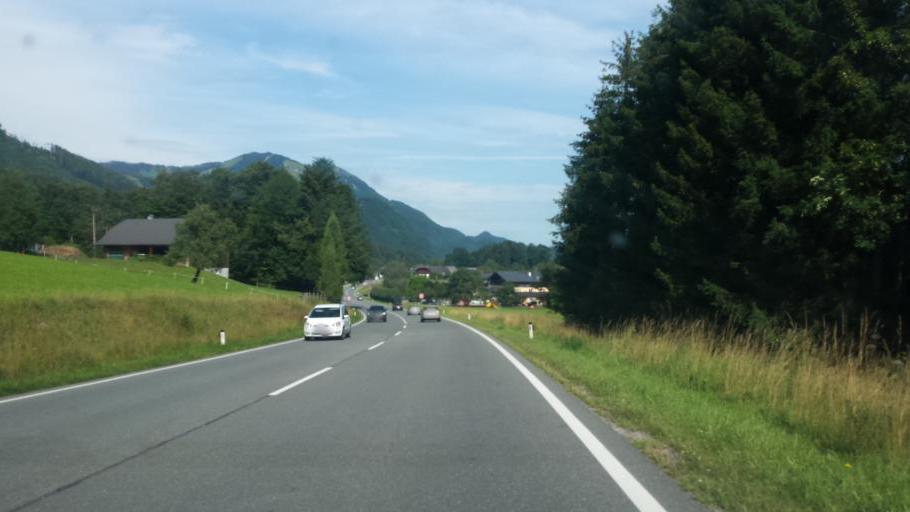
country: AT
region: Upper Austria
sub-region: Politischer Bezirk Gmunden
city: Sankt Wolfgang im Salzkammergut
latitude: 47.7195
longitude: 13.4335
